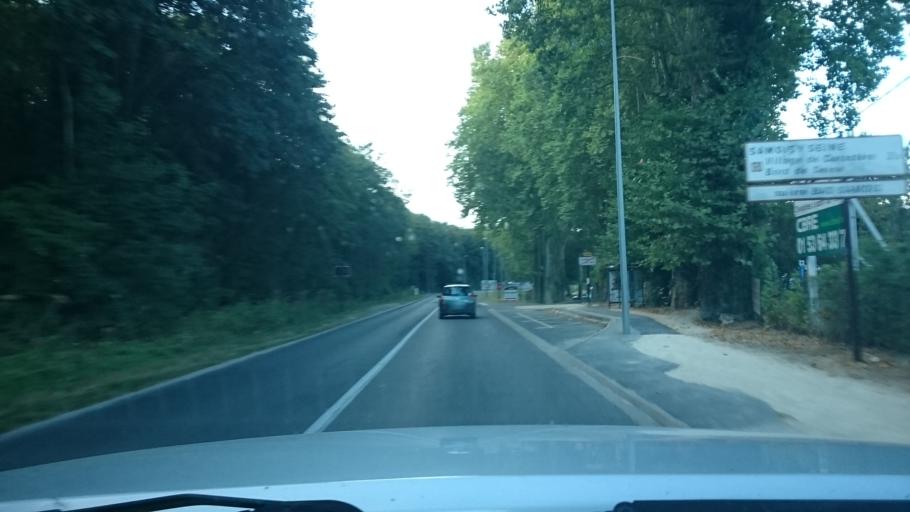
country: FR
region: Ile-de-France
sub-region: Departement de Seine-et-Marne
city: Samoreau
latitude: 48.4271
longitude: 2.7431
